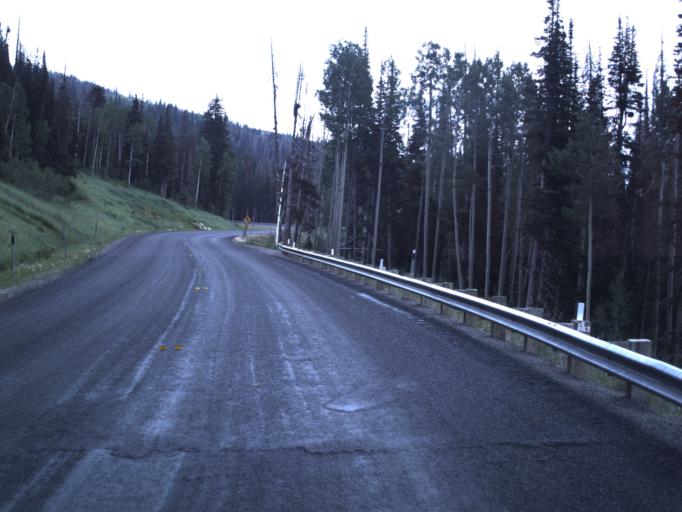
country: US
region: Utah
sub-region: Summit County
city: Francis
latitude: 40.4965
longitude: -111.0395
